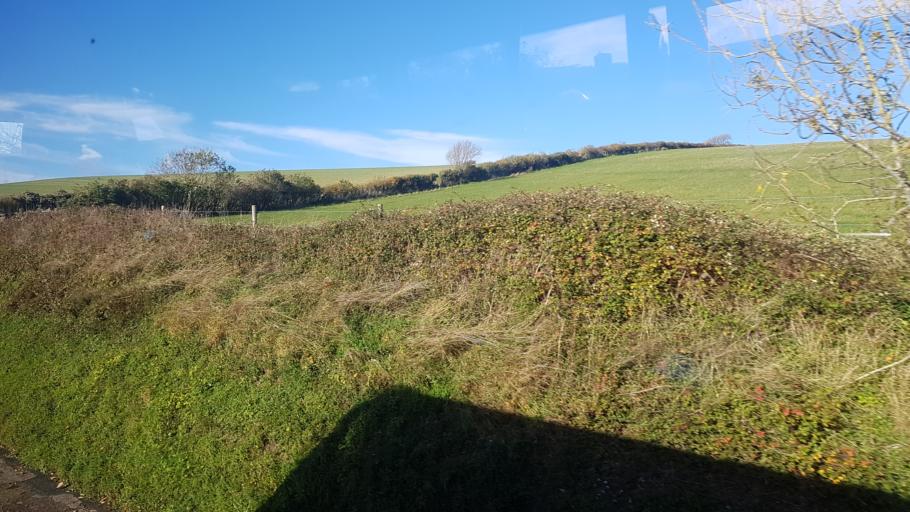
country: GB
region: England
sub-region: Isle of Wight
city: Newport
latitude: 50.6827
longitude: -1.3311
